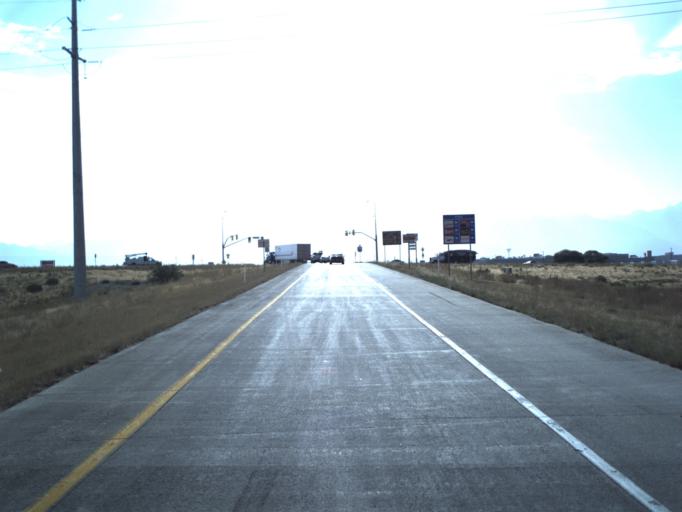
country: US
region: Utah
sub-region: Salt Lake County
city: West Valley City
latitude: 40.7251
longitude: -112.0271
